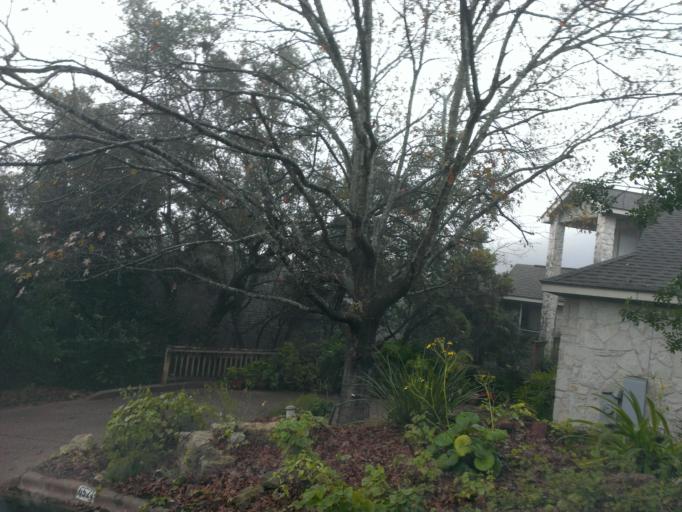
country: US
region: Texas
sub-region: Williamson County
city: Jollyville
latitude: 30.3733
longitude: -97.7928
